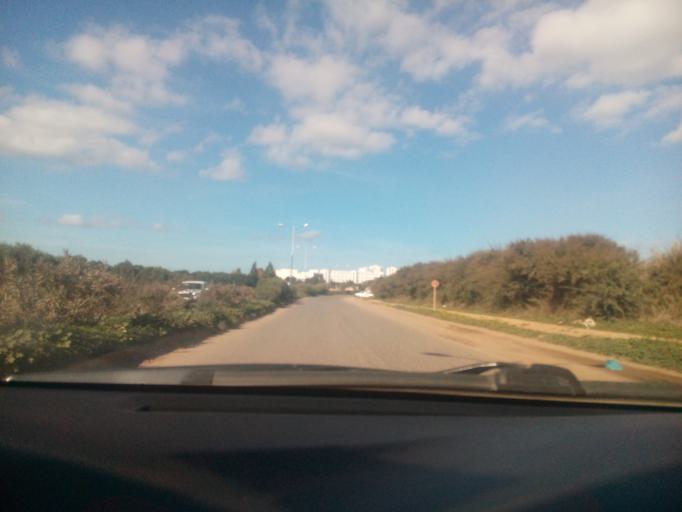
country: DZ
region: Oran
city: Bir el Djir
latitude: 35.6876
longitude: -0.5744
